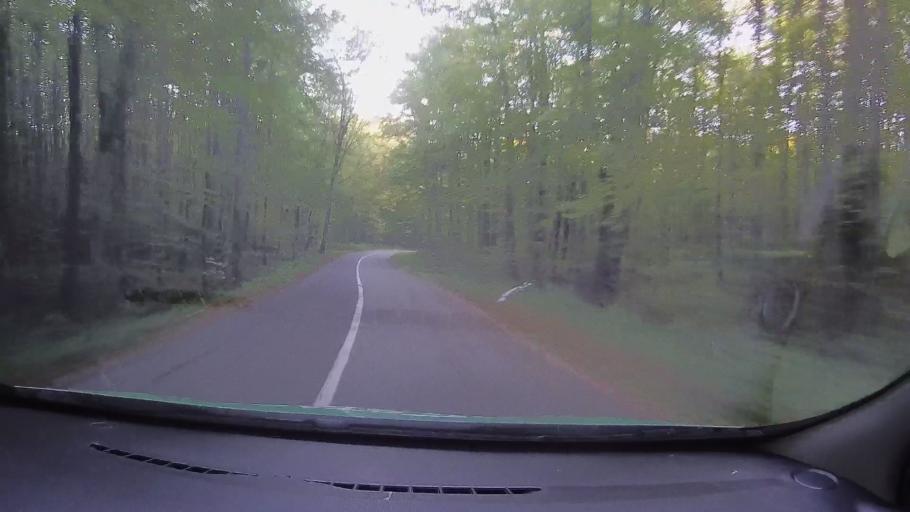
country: RO
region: Timis
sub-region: Comuna Nadrag
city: Nadrag
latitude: 45.6786
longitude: 22.1583
